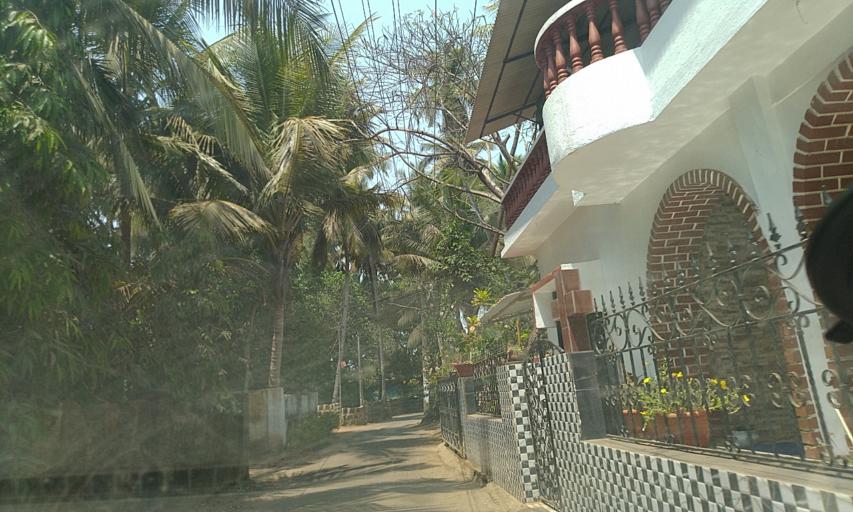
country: IN
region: Goa
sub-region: North Goa
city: Saligao
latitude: 15.5500
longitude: 73.7859
